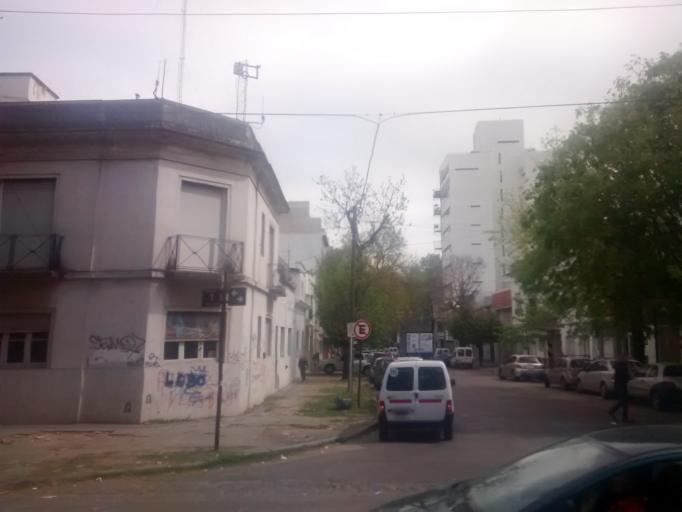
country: AR
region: Buenos Aires
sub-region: Partido de La Plata
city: La Plata
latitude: -34.9145
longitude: -57.9365
